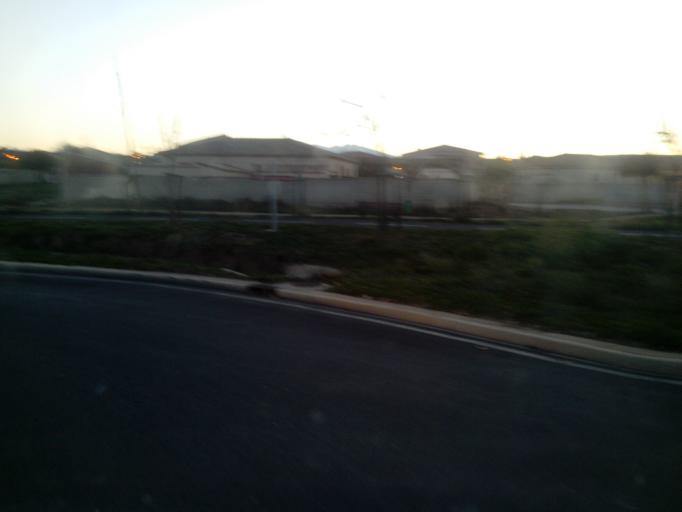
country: FR
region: Languedoc-Roussillon
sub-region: Departement des Pyrenees-Orientales
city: Peyrestortes
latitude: 42.7729
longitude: 2.8415
